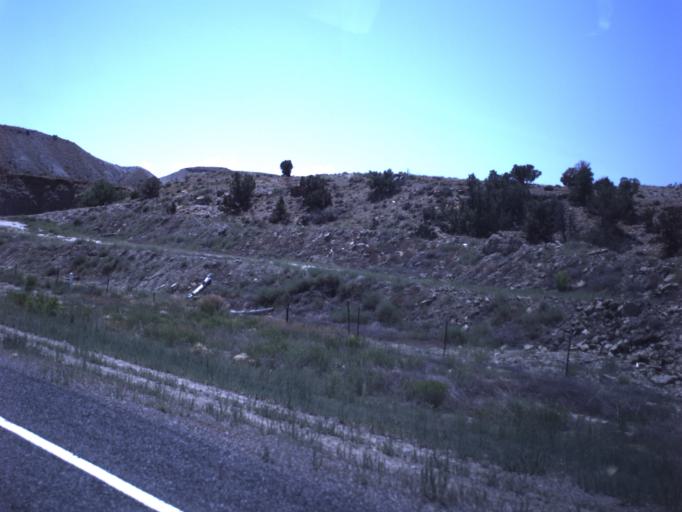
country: US
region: Utah
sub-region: Emery County
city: Orangeville
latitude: 39.2363
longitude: -111.0871
